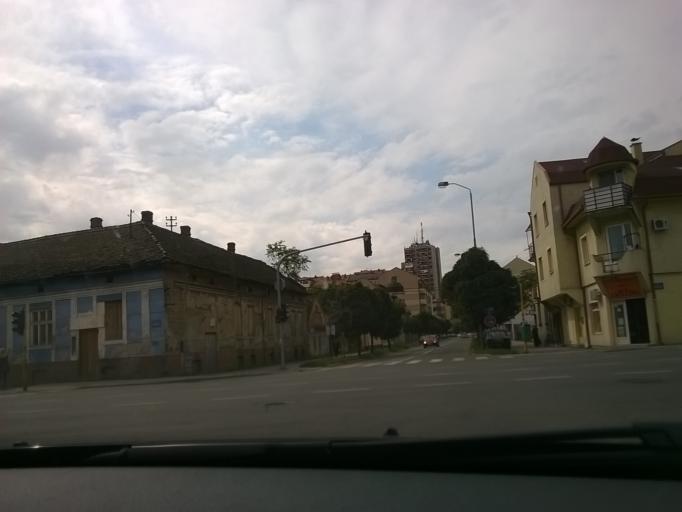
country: RS
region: Autonomna Pokrajina Vojvodina
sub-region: Juznobanatski Okrug
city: Pancevo
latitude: 44.8743
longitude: 20.6455
